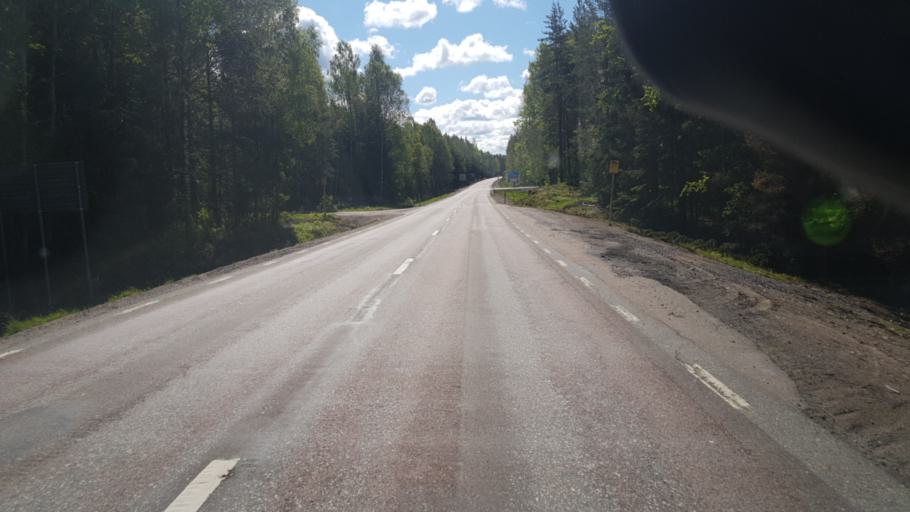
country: SE
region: Vaermland
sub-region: Arvika Kommun
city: Arvika
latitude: 59.5438
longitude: 12.7449
